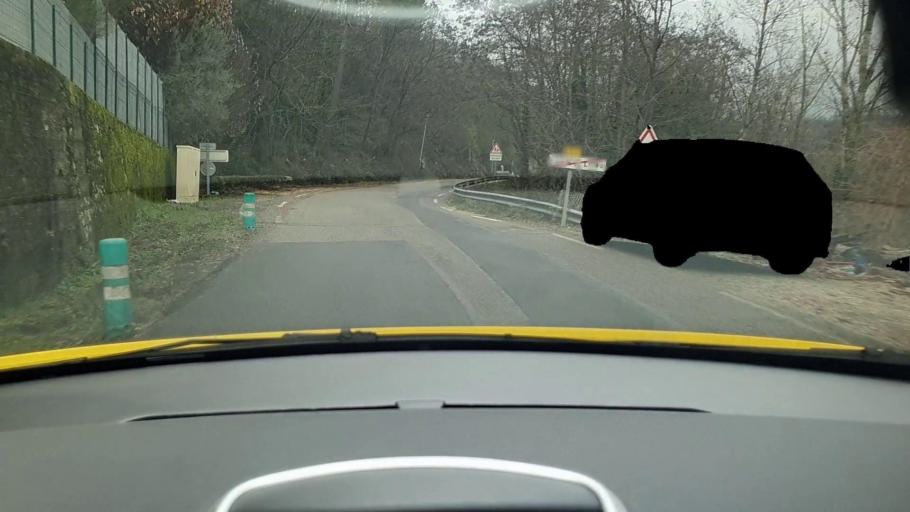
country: FR
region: Languedoc-Roussillon
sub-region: Departement du Gard
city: Besseges
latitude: 44.3054
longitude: 4.0931
